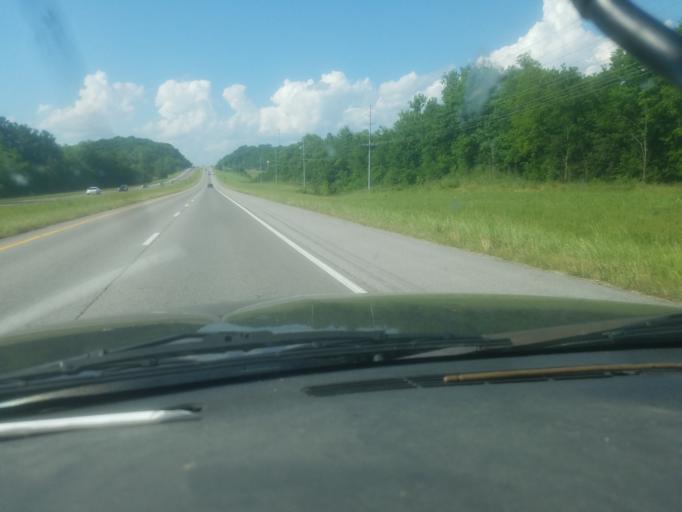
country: US
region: Tennessee
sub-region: Maury County
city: Mount Pleasant
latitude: 35.5250
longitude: -87.2223
